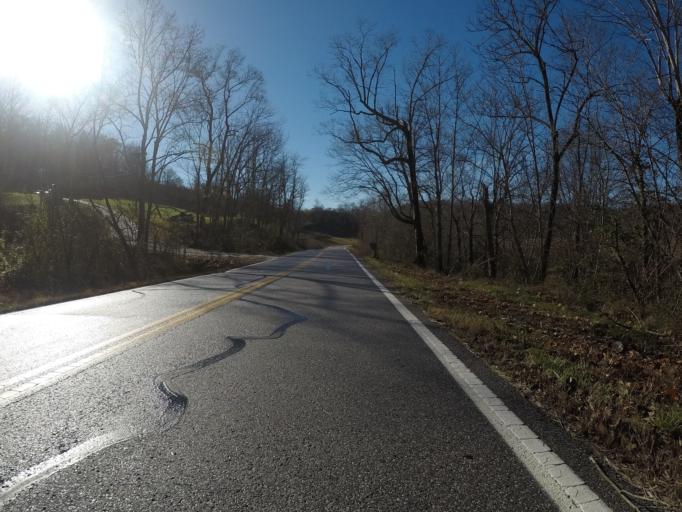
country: US
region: West Virginia
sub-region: Cabell County
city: Huntington
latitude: 38.4743
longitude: -82.4431
